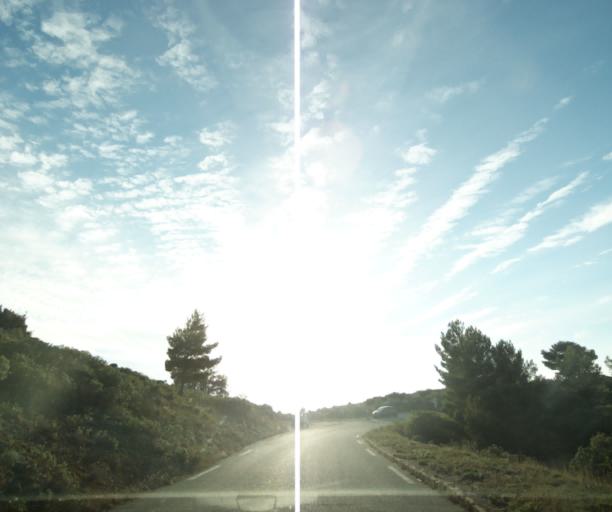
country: FR
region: Provence-Alpes-Cote d'Azur
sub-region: Departement des Bouches-du-Rhone
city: Cassis
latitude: 43.1908
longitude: 5.5565
